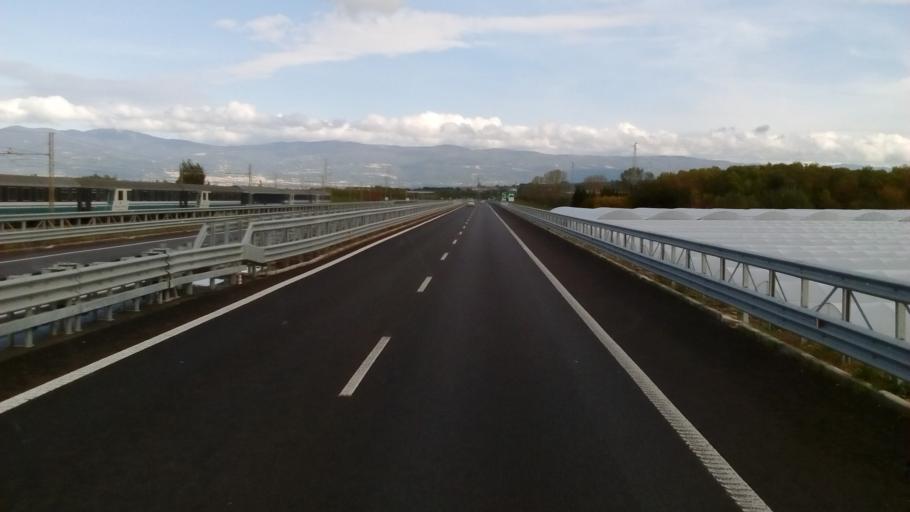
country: IT
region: Calabria
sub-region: Provincia di Catanzaro
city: Acconia
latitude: 38.8481
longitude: 16.2671
